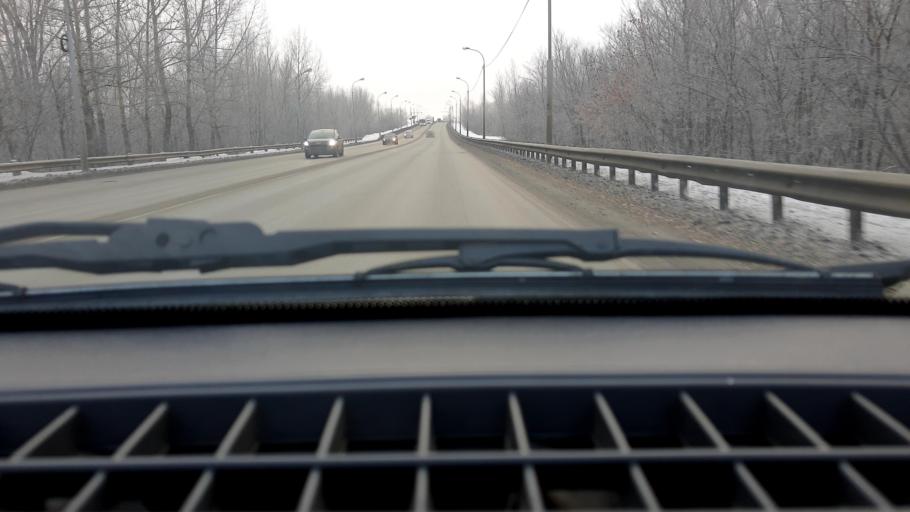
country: RU
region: Bashkortostan
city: Iglino
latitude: 54.7920
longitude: 56.2115
